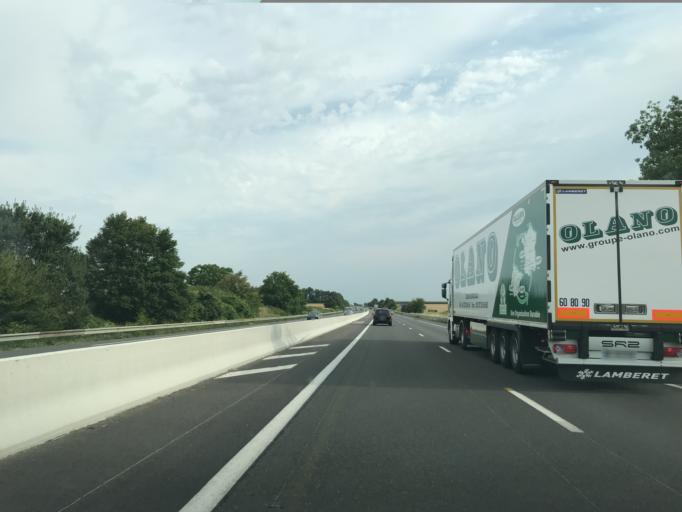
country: FR
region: Centre
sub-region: Departement d'Indre-et-Loire
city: Sainte-Maure-de-Touraine
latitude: 47.0796
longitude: 0.5861
